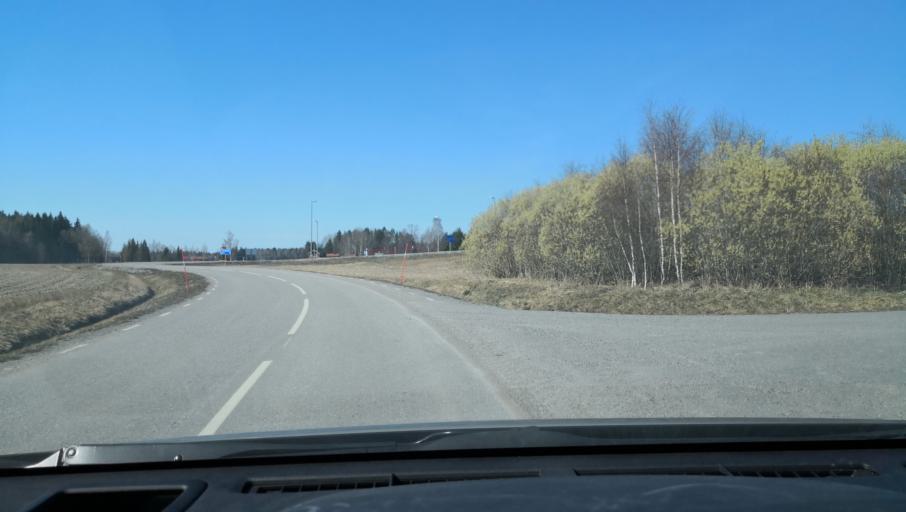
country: SE
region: Vaestmanland
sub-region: Sala Kommun
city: Sala
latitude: 59.9075
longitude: 16.5313
